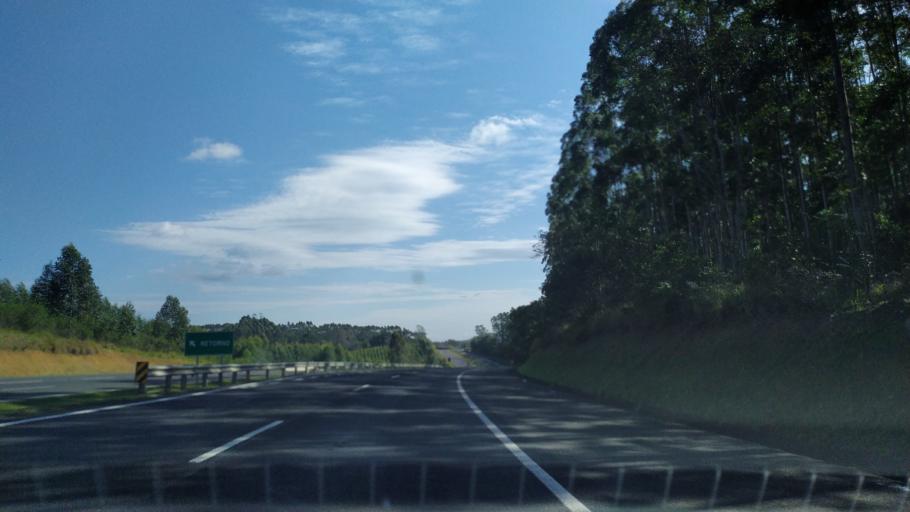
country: BR
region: Parana
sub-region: Telemaco Borba
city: Telemaco Borba
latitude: -24.4247
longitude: -50.7704
